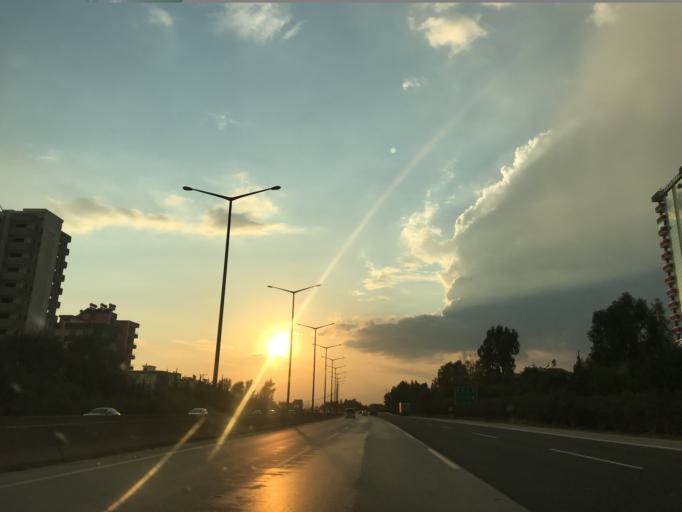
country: TR
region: Adana
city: Seyhan
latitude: 37.0326
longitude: 35.2439
